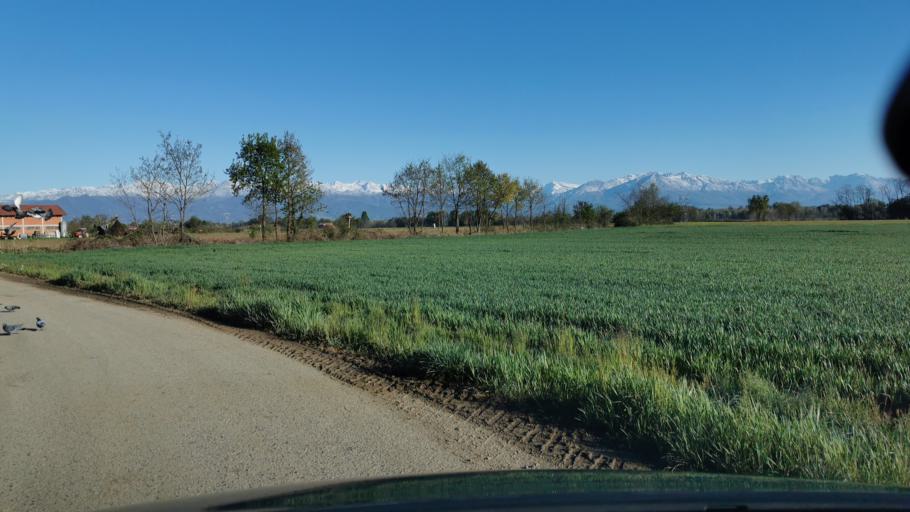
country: IT
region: Piedmont
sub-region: Provincia di Torino
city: Lombardore
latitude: 45.2168
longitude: 7.7107
